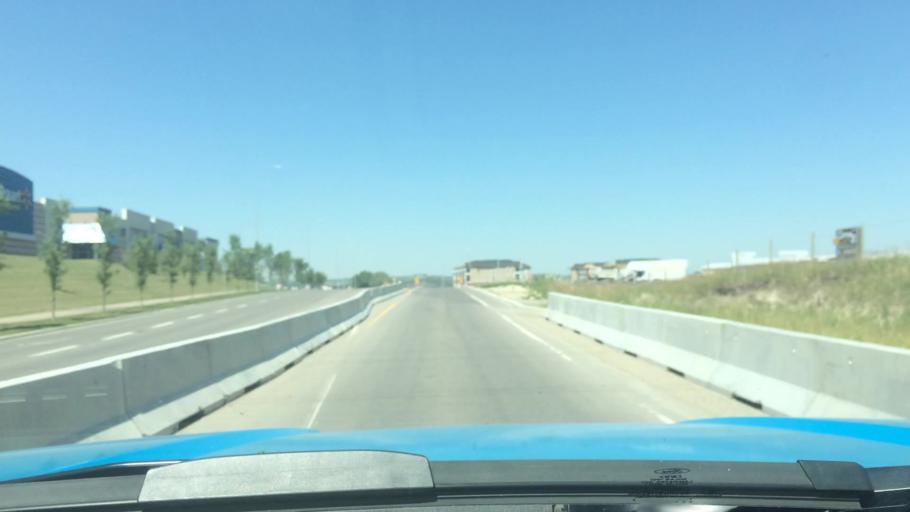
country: CA
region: Alberta
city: Calgary
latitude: 51.1686
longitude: -114.1413
